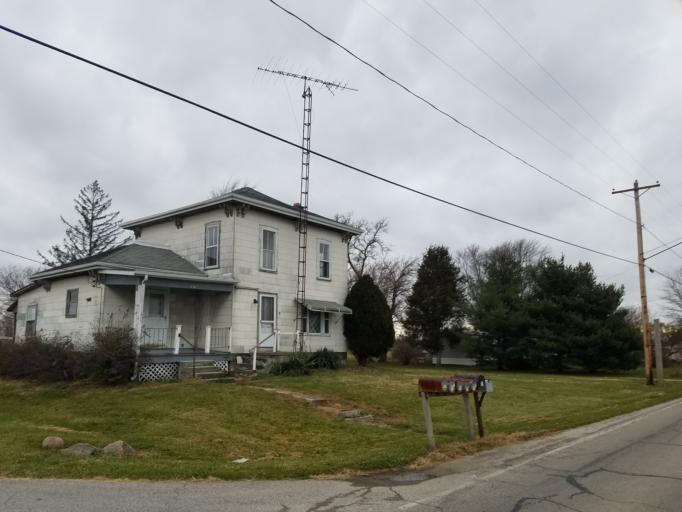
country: US
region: Ohio
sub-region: Crawford County
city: Galion
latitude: 40.6657
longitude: -82.9100
